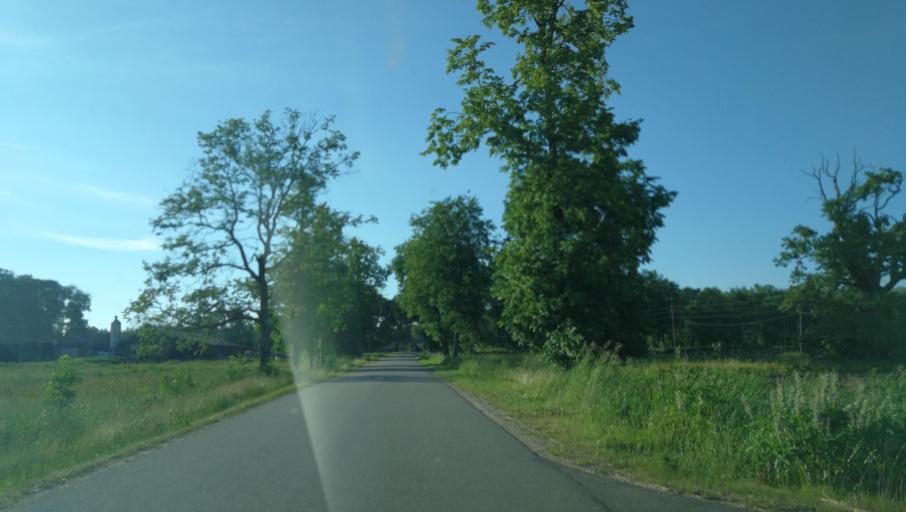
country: LV
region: Pargaujas
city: Stalbe
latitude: 57.3569
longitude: 25.0901
